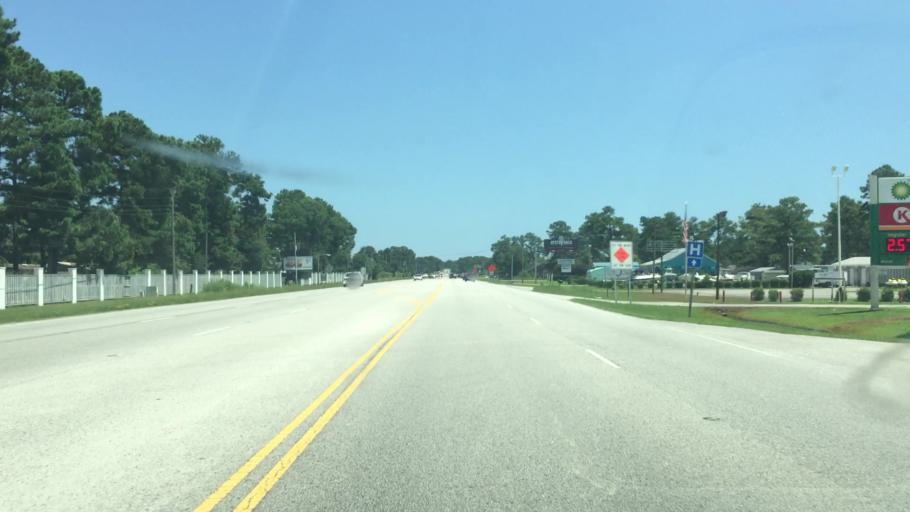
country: US
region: South Carolina
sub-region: Horry County
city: North Myrtle Beach
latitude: 33.8711
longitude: -78.6716
